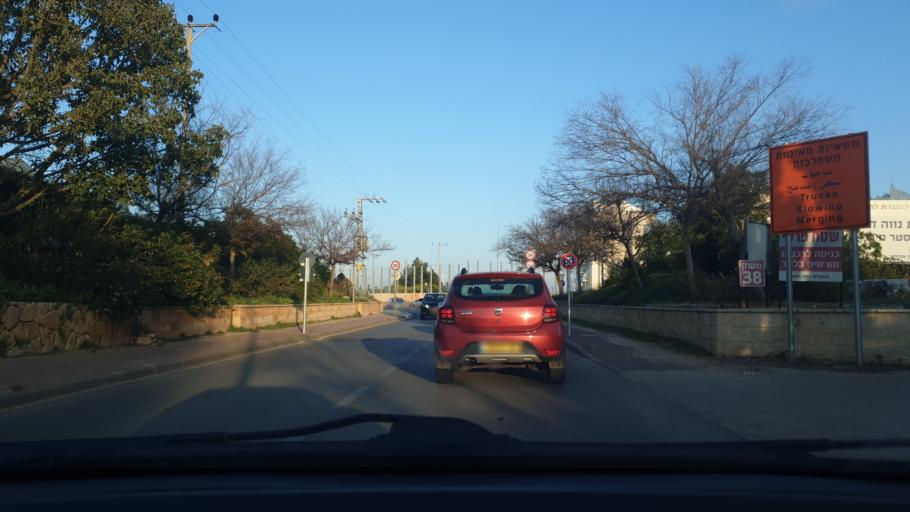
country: IL
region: Central District
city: Ramla
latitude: 31.9355
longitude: 34.8506
